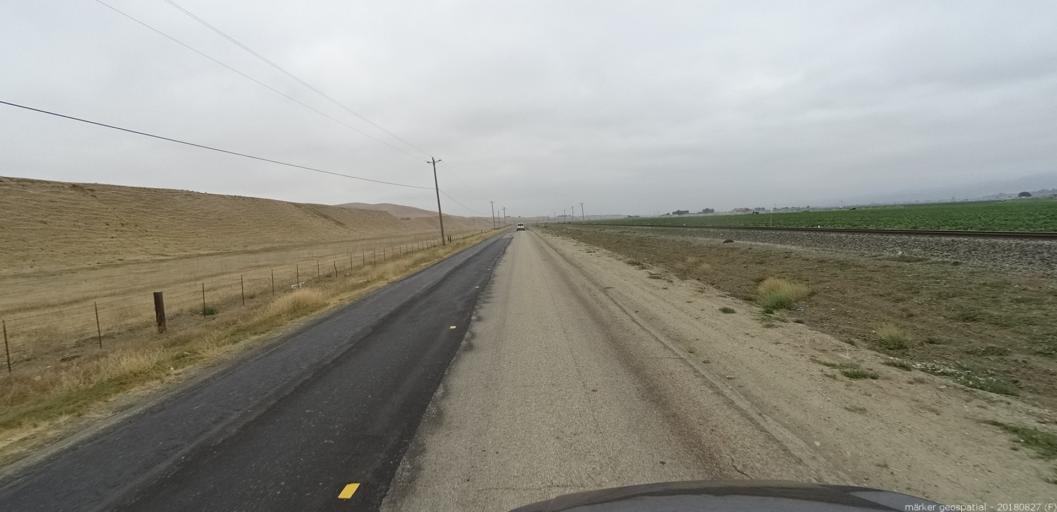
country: US
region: California
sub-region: Monterey County
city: Greenfield
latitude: 36.3097
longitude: -121.1673
